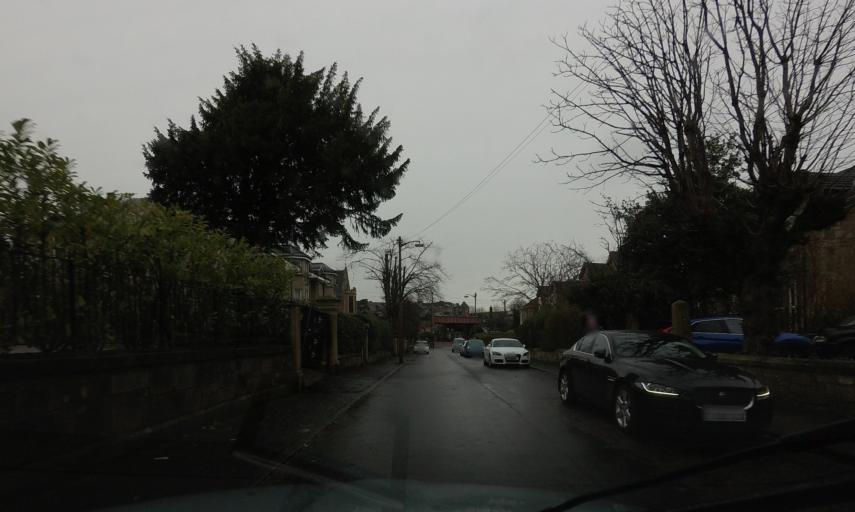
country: GB
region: Scotland
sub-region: East Renfrewshire
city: Giffnock
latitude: 55.8277
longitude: -4.2901
